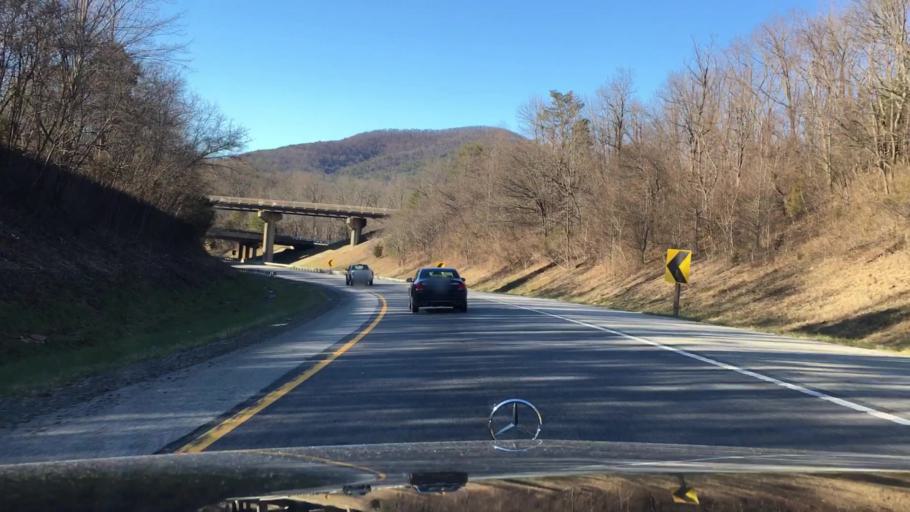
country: US
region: Virginia
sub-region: Roanoke County
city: Hollins
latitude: 37.3397
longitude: -79.9959
